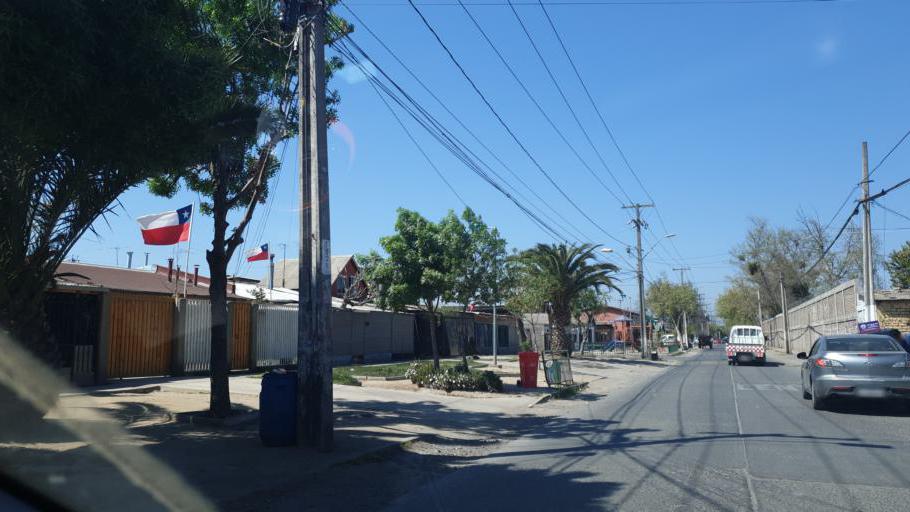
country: CL
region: Santiago Metropolitan
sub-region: Provincia de Talagante
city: Talagante
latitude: -33.6543
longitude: -70.9259
